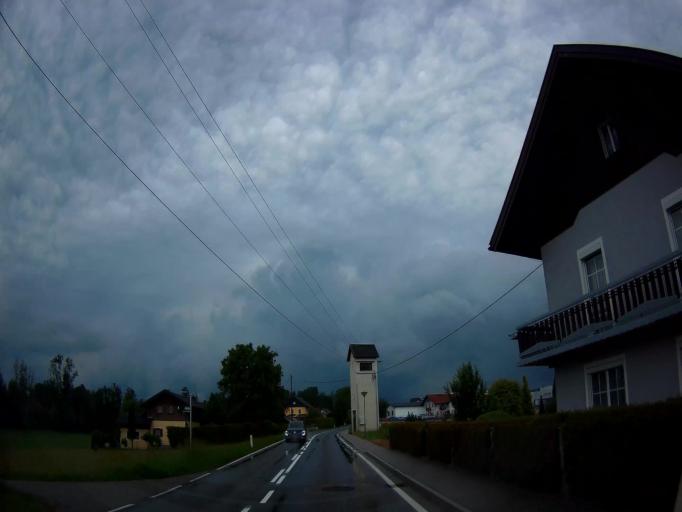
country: AT
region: Salzburg
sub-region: Politischer Bezirk Salzburg-Umgebung
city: Mattsee
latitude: 48.0536
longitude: 13.1502
